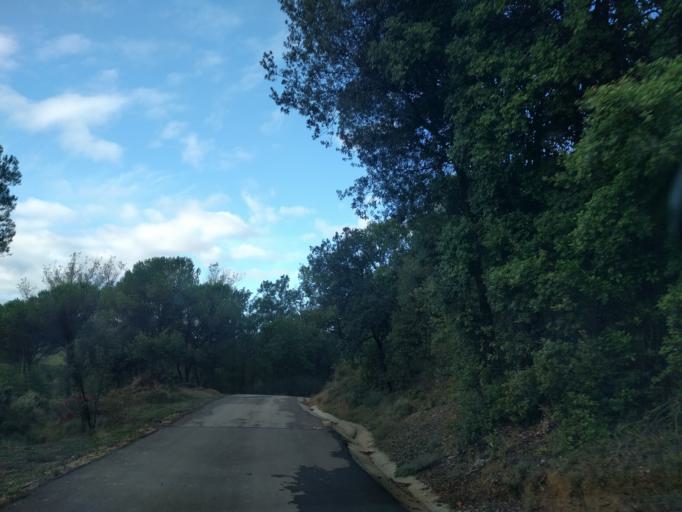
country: ES
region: Catalonia
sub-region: Provincia de Girona
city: Sant Aniol de Finestres
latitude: 42.0391
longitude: 2.6289
